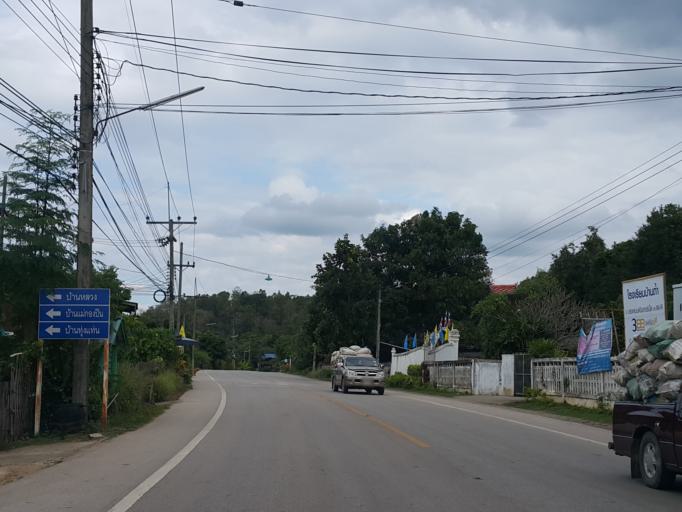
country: TH
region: Lampang
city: Chae Hom
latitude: 18.5999
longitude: 99.4793
